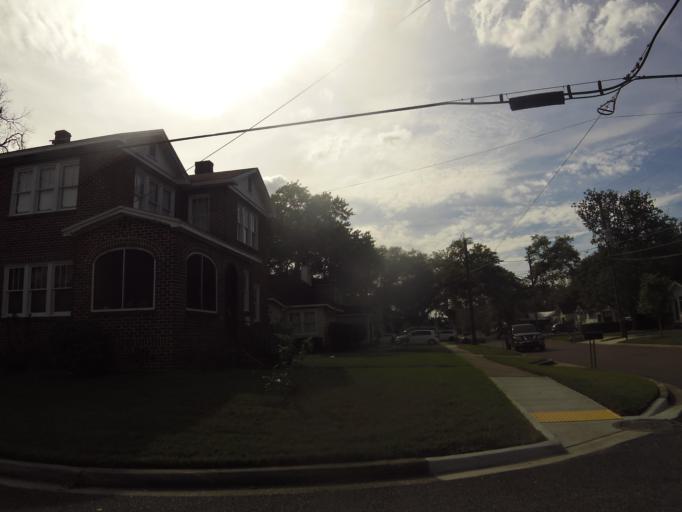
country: US
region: Florida
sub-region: Duval County
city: Jacksonville
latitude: 30.3144
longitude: -81.7245
